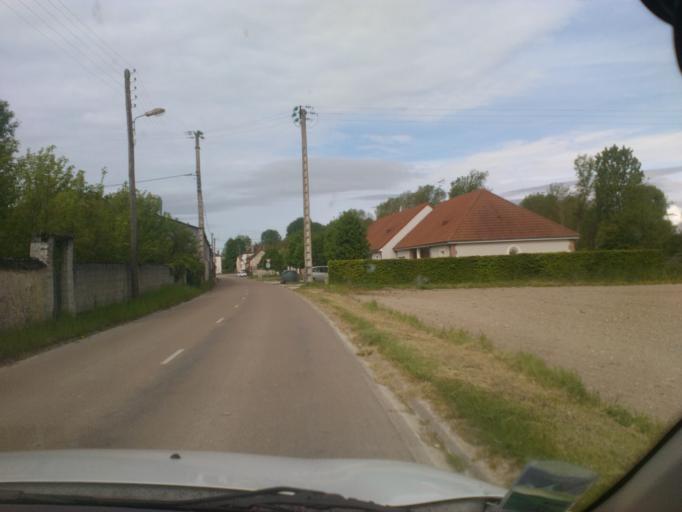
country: FR
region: Champagne-Ardenne
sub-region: Departement de l'Aube
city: Marigny-le-Chatel
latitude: 48.3486
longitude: 3.6376
